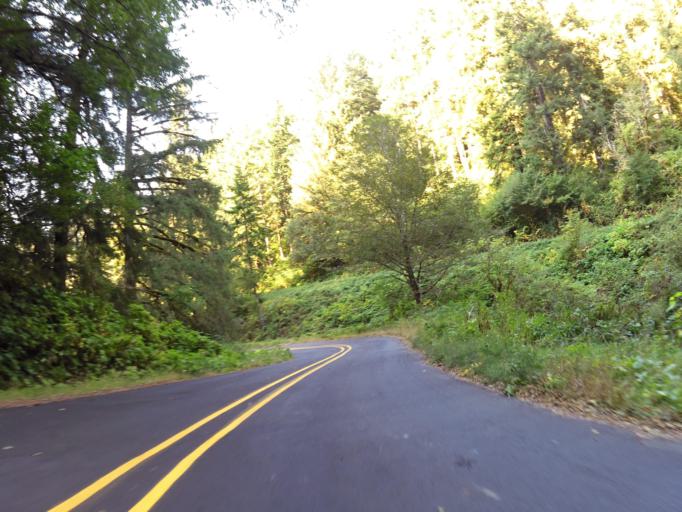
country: US
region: Oregon
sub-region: Lincoln County
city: Rose Lodge
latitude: 45.0351
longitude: -123.9113
